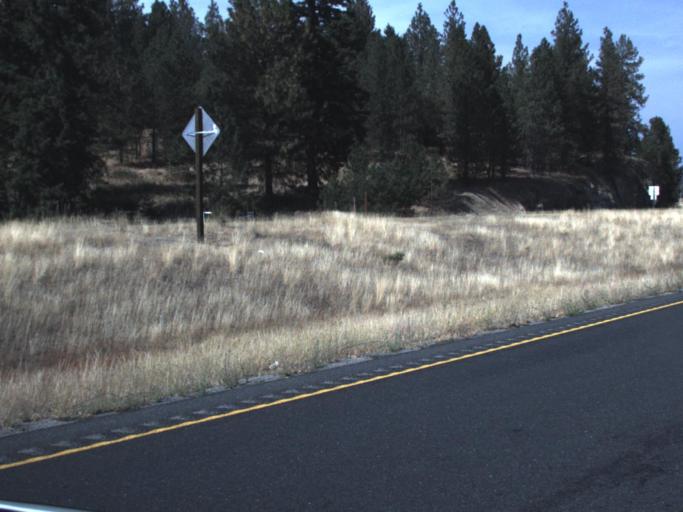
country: US
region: Washington
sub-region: Spokane County
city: Deer Park
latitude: 48.0451
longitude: -117.3446
